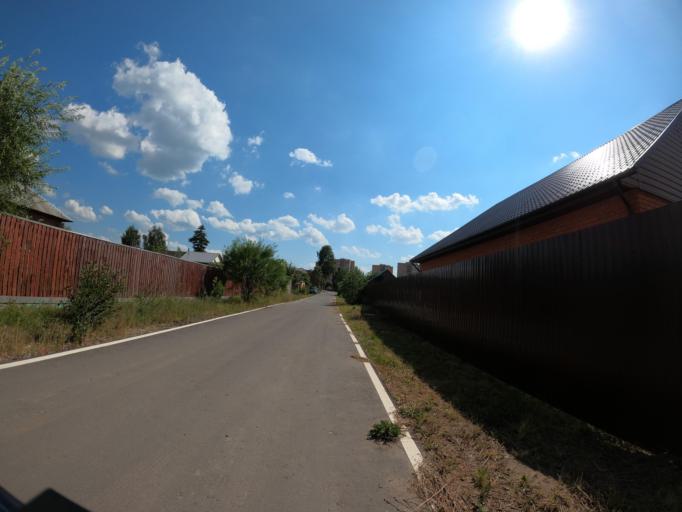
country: RU
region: Moskovskaya
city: Peski
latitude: 55.2546
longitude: 38.7686
